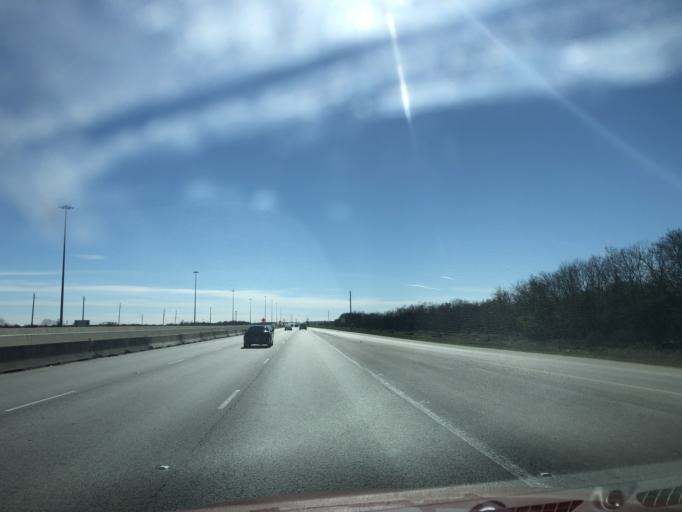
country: US
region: Texas
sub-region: Brazoria County
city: Brookside Village
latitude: 29.6398
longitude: -95.3877
